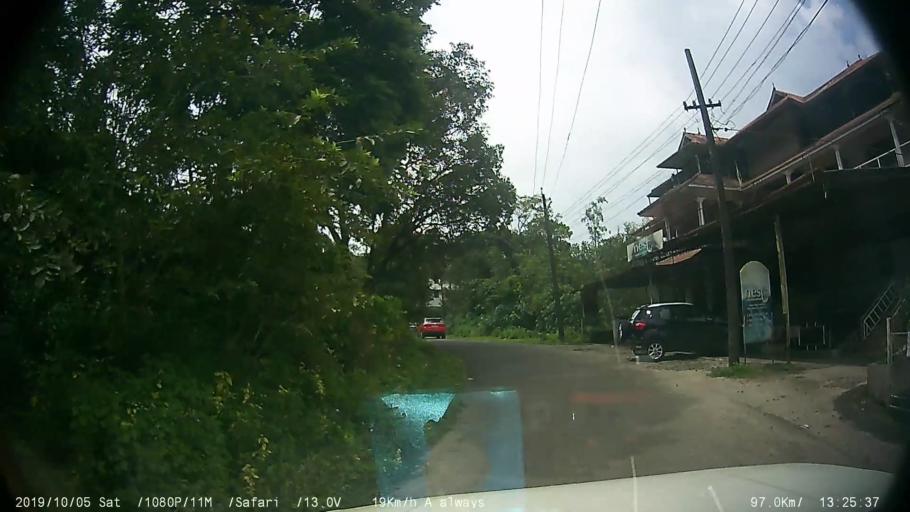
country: IN
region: Kerala
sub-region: Kottayam
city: Erattupetta
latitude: 9.5786
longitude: 76.9699
